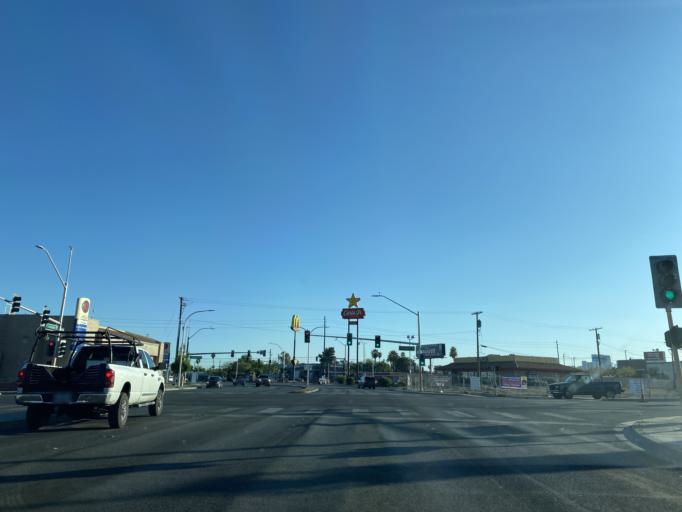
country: US
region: Nevada
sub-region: Clark County
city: Las Vegas
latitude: 36.1601
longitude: -115.1183
